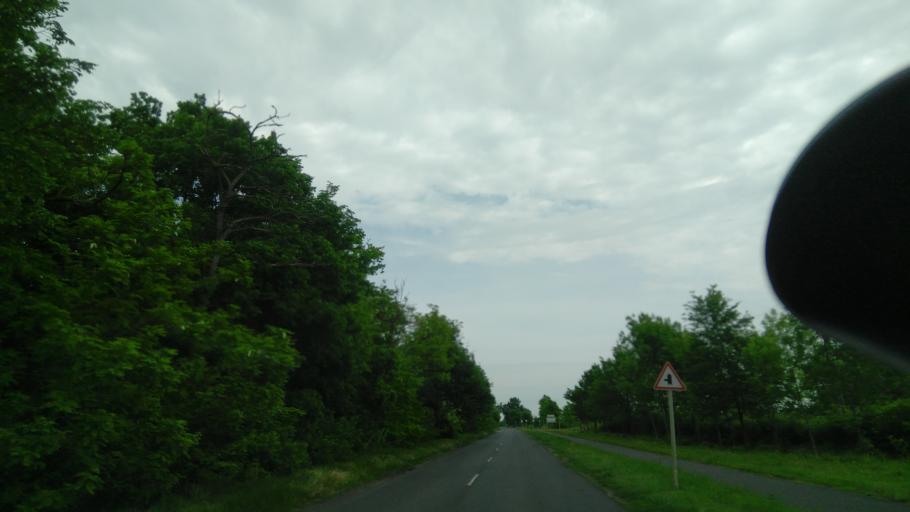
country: HU
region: Bekes
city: Szeghalom
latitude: 47.0507
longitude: 21.1919
